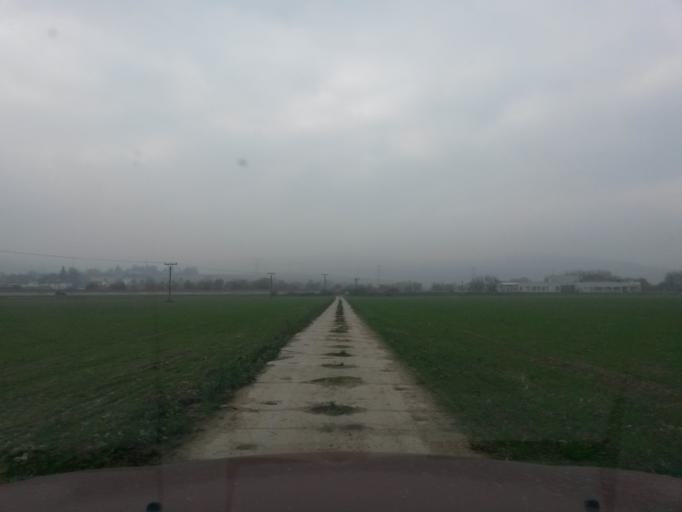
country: SK
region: Kosicky
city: Kosice
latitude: 48.8562
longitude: 21.2760
